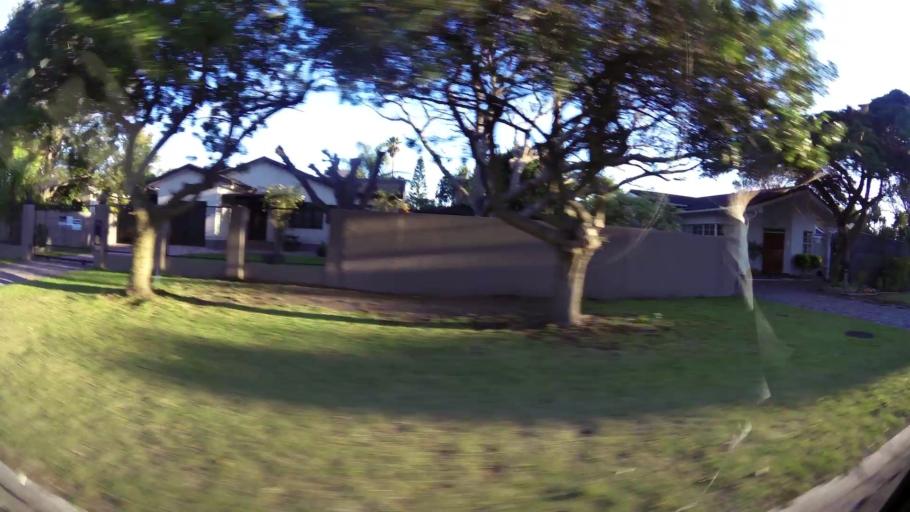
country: ZA
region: Eastern Cape
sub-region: Nelson Mandela Bay Metropolitan Municipality
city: Port Elizabeth
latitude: -33.9732
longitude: 25.4999
